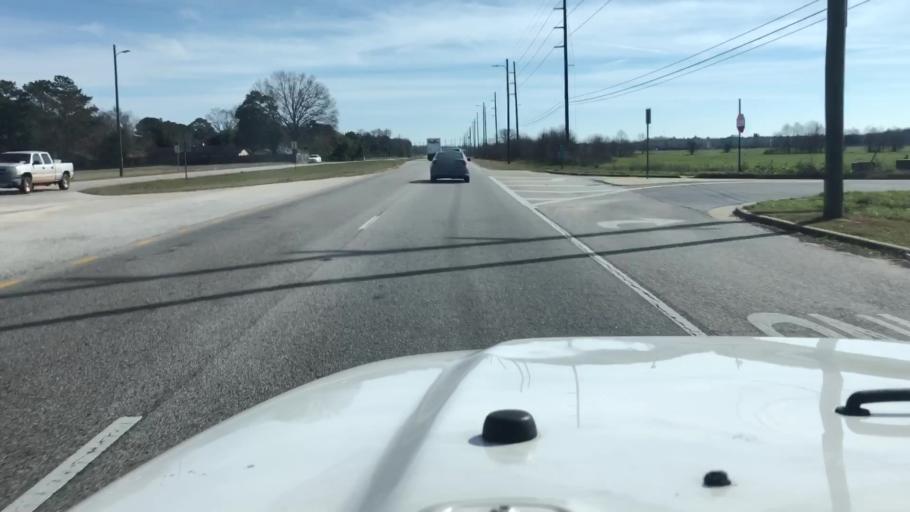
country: US
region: Alabama
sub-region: Montgomery County
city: Pike Road
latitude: 32.3778
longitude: -86.1547
